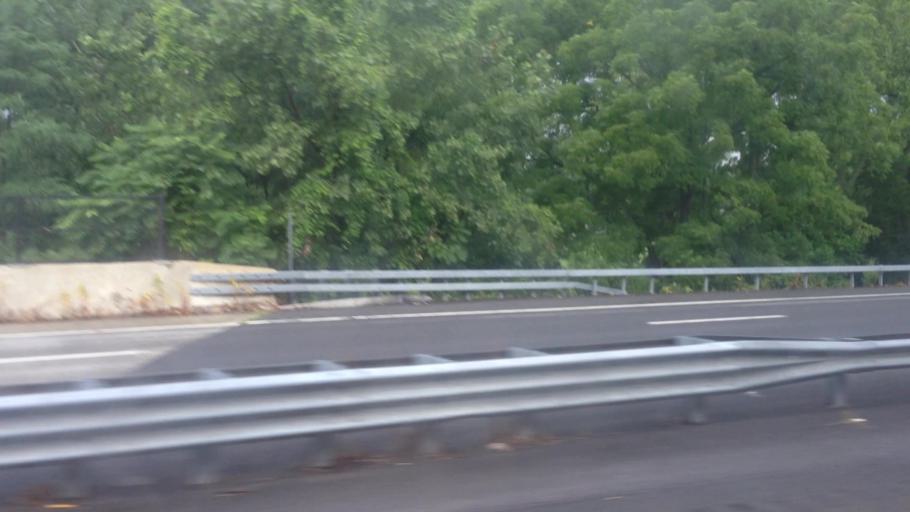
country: US
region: New York
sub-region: Ulster County
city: Kingston
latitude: 41.9347
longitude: -74.0117
